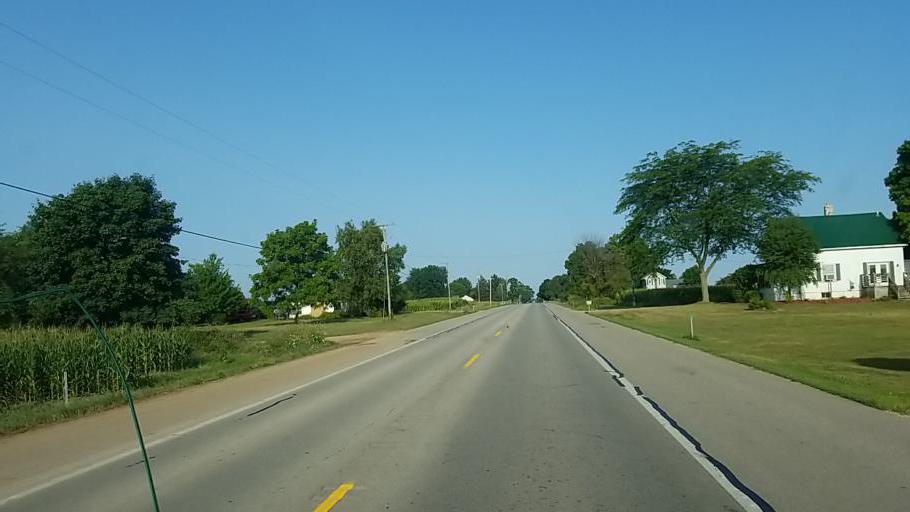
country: US
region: Michigan
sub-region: Newaygo County
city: Fremont
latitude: 43.4673
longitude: -86.0128
